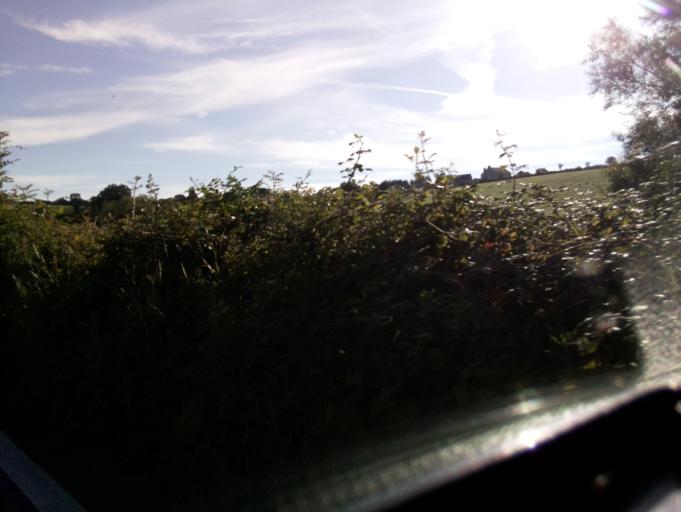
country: GB
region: England
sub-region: Bath and North East Somerset
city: Keynsham
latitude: 51.4326
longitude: -2.5054
